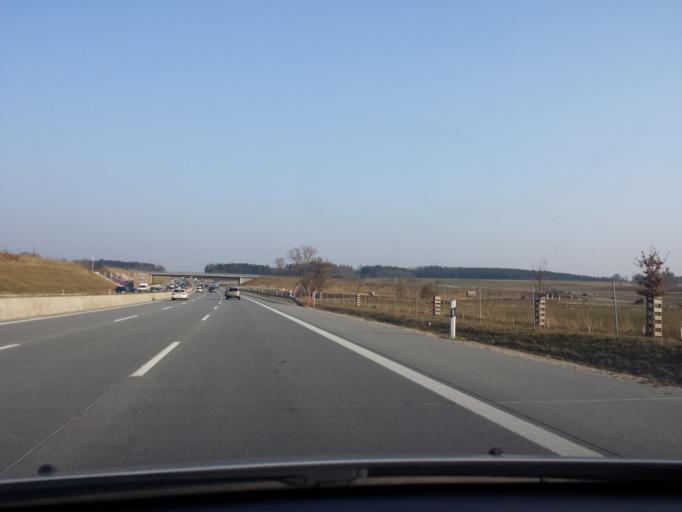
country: DE
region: Bavaria
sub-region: Upper Bavaria
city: Odelzhausen
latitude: 48.2962
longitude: 11.2272
